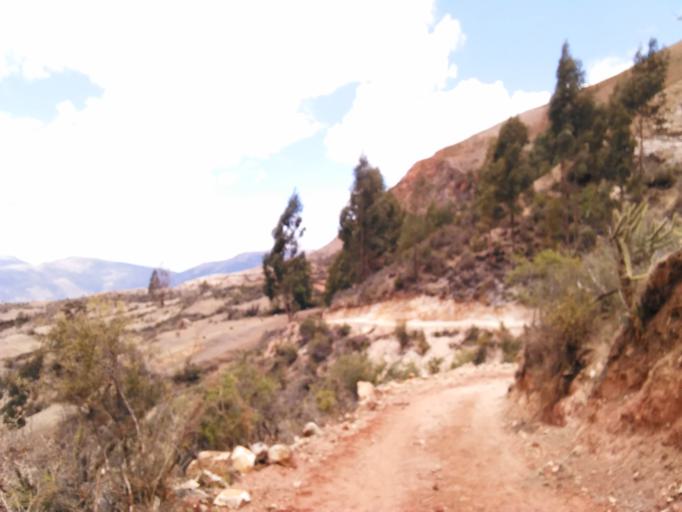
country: PE
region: Ayacucho
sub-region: Provincia de Victor Fajardo
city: Canaria
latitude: -13.8852
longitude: -73.9444
